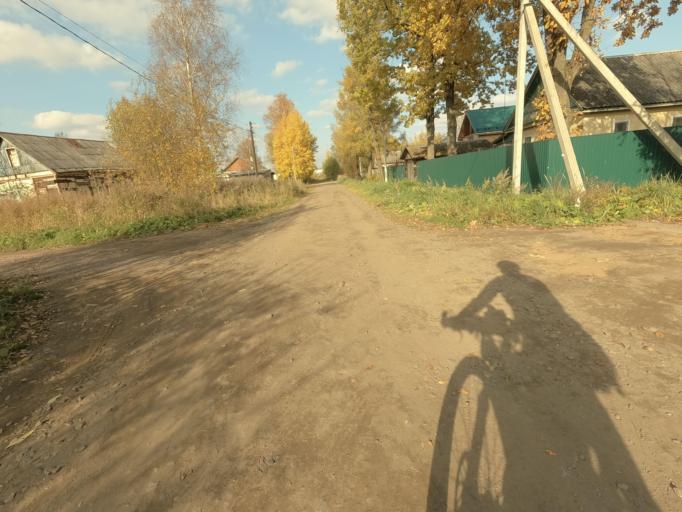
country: RU
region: Leningrad
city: Mga
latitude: 59.7517
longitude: 31.0732
